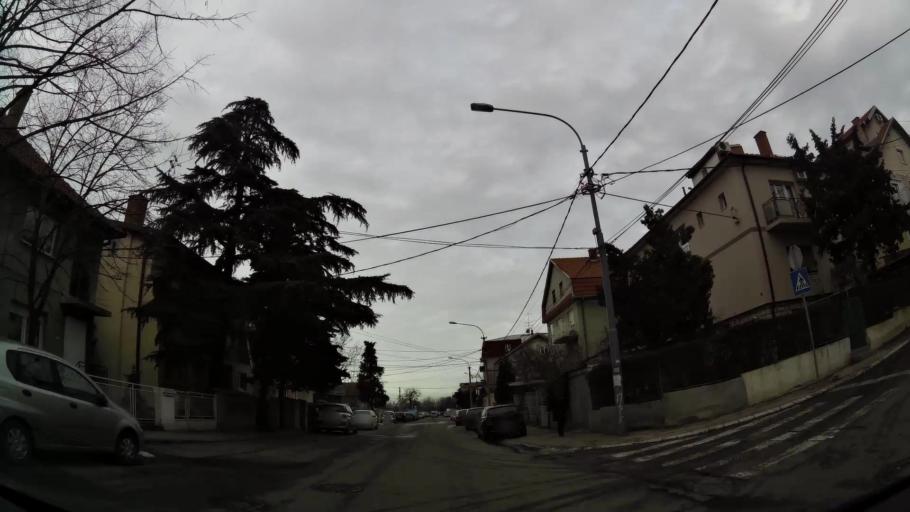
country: RS
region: Central Serbia
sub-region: Belgrade
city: Cukarica
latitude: 44.7657
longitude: 20.4100
